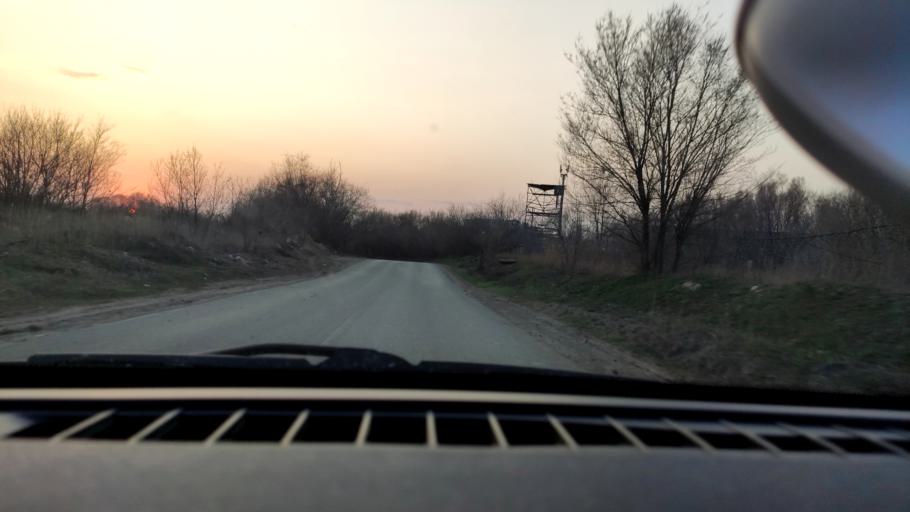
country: RU
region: Samara
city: Smyshlyayevka
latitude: 53.2069
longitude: 50.3120
